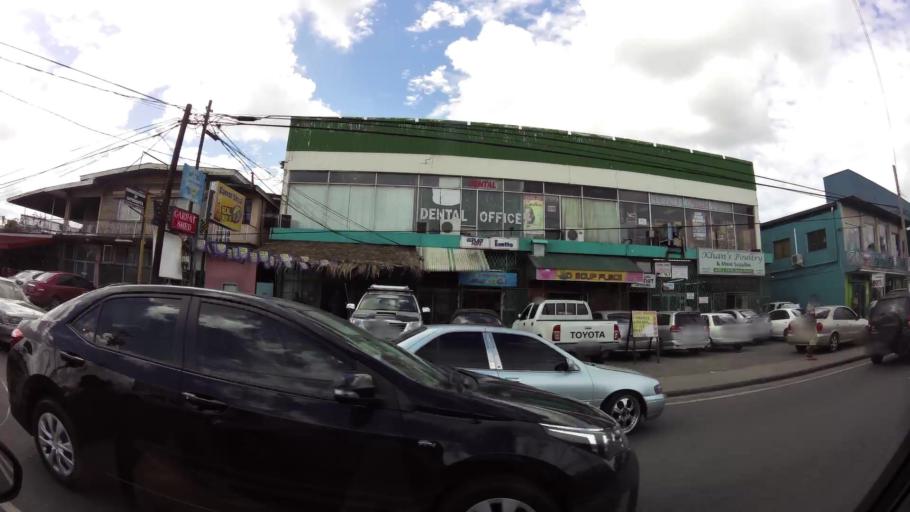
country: TT
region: City of San Fernando
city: Marabella
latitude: 10.3026
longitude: -61.4494
